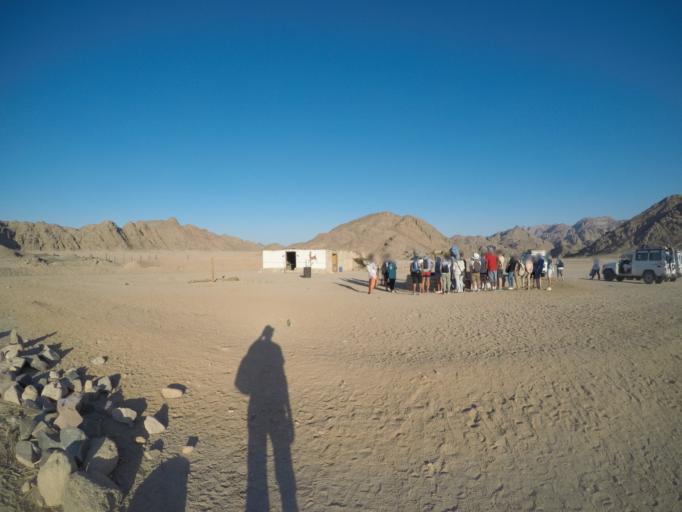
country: EG
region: Red Sea
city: El Gouna
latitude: 27.1511
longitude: 33.5445
